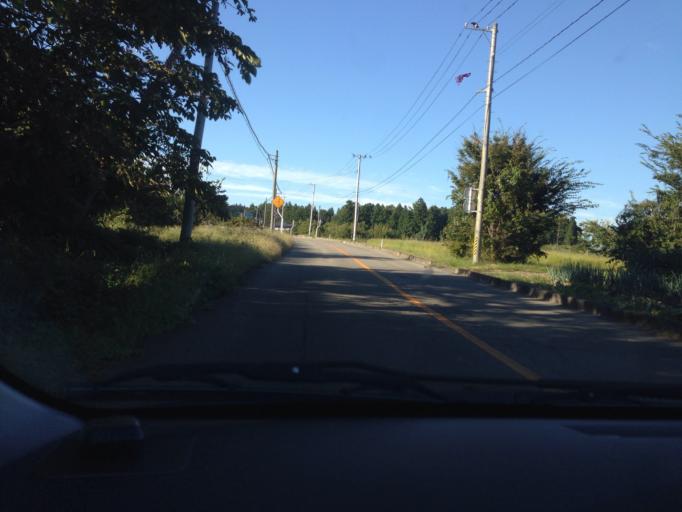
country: JP
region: Fukushima
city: Kitakata
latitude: 37.5916
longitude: 139.8107
